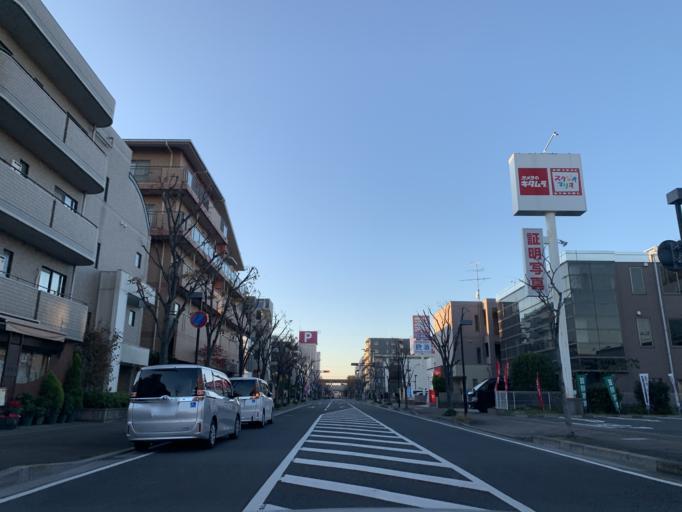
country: JP
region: Tokyo
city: Urayasu
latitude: 35.6905
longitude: 139.9299
